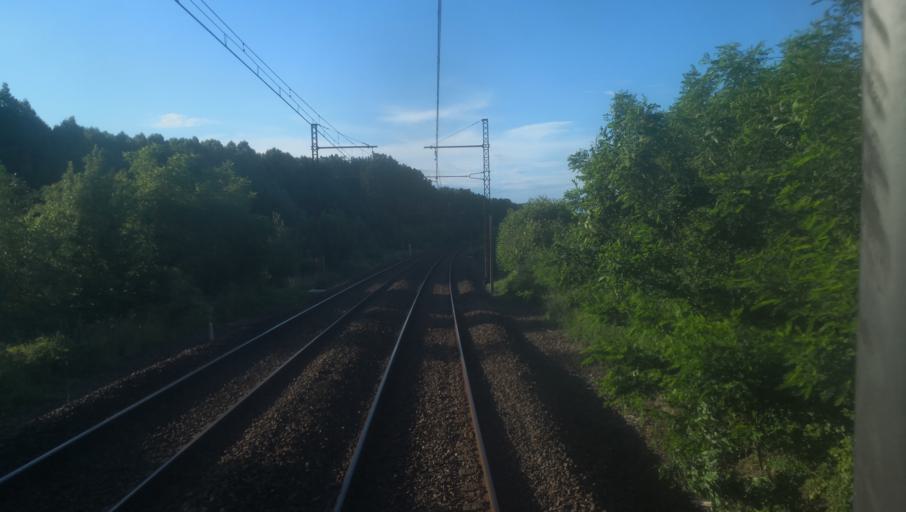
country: FR
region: Centre
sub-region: Departement de l'Indre
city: Sainte-Lizaigne
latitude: 47.0445
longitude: 2.0331
